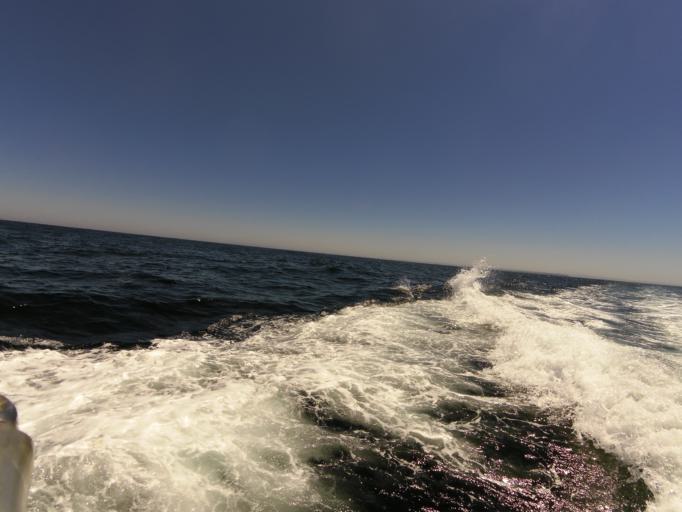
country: PT
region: Leiria
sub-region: Peniche
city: Peniche
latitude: 39.3943
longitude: -9.4785
